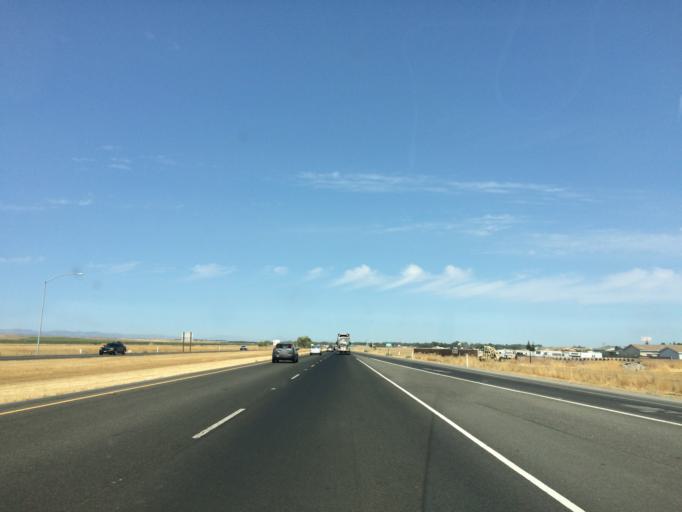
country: US
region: California
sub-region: Yolo County
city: Dunnigan
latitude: 38.8627
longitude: -121.9550
